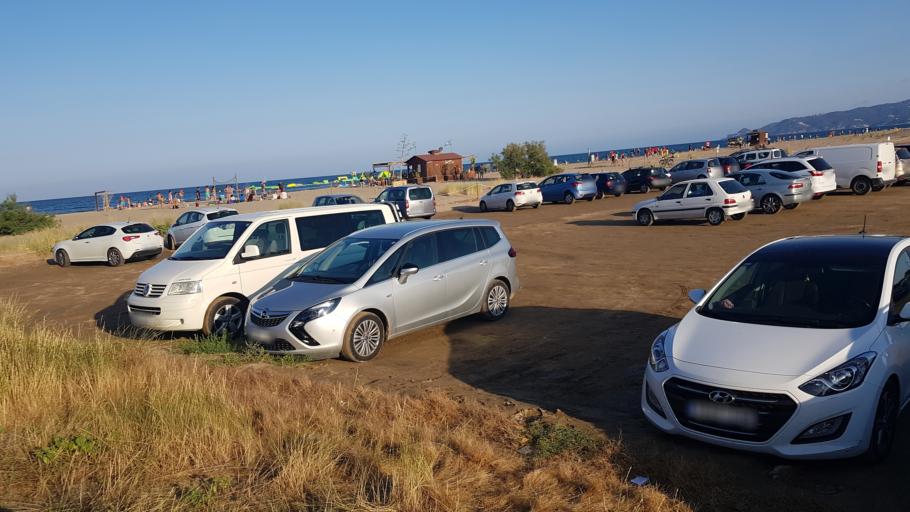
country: ES
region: Catalonia
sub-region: Provincia de Girona
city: Torroella de Montgri
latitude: 42.0474
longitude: 3.1965
